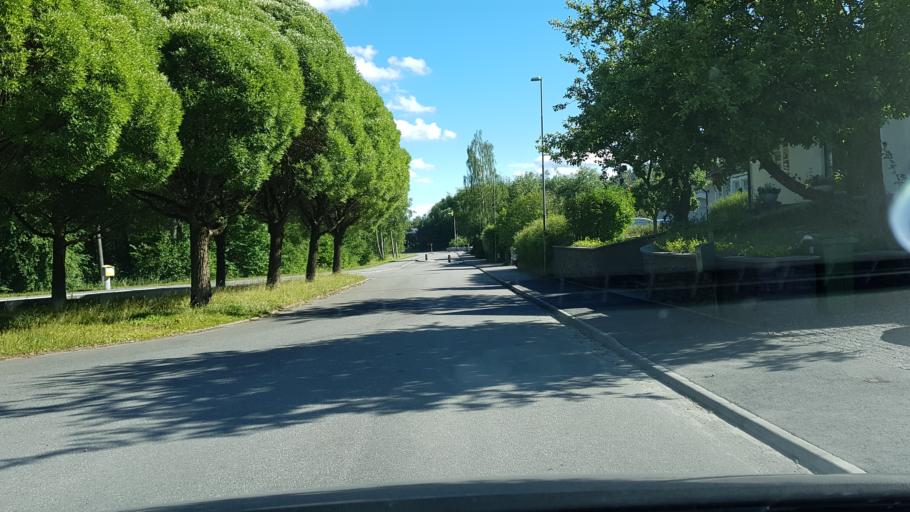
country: SE
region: Stockholm
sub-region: Upplands-Bro Kommun
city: Kungsaengen
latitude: 59.4771
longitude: 17.8043
